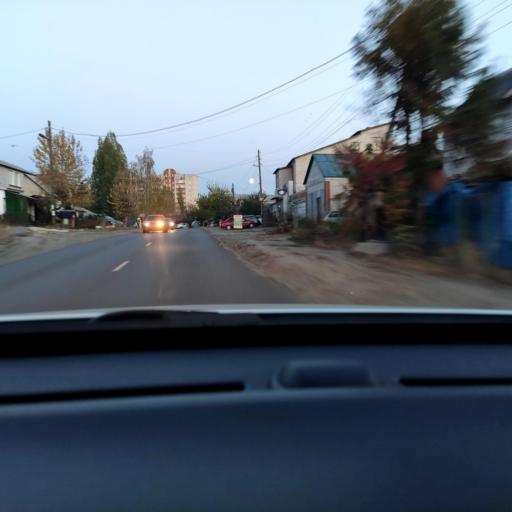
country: RU
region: Voronezj
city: Voronezh
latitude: 51.6976
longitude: 39.2609
